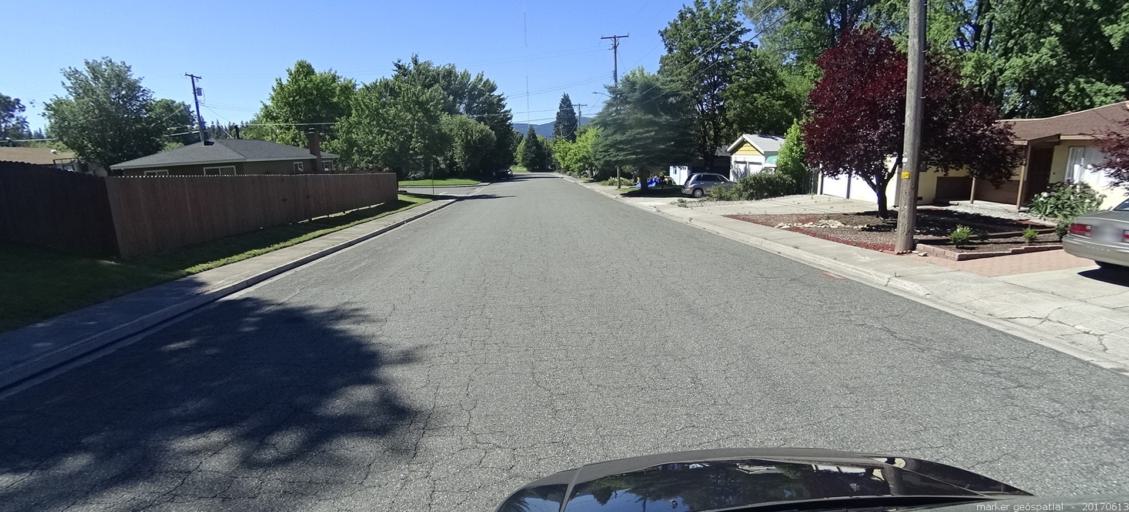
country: US
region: California
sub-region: Siskiyou County
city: Mount Shasta
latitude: 41.3214
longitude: -122.3105
